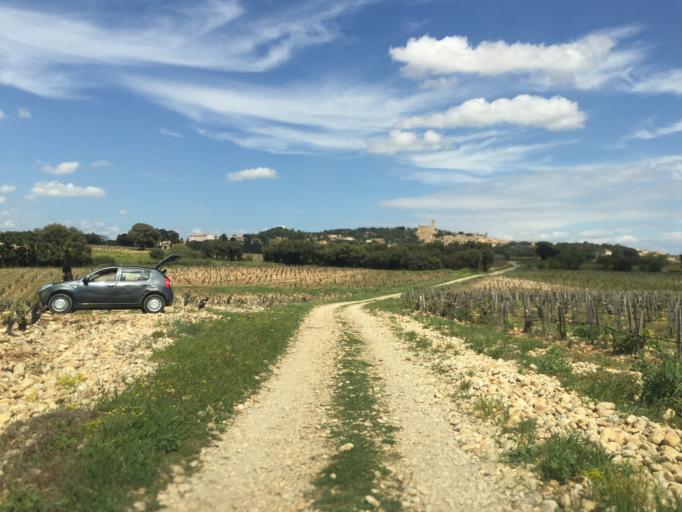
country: FR
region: Provence-Alpes-Cote d'Azur
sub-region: Departement du Vaucluse
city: Chateauneuf-du-Pape
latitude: 44.0466
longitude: 4.8227
